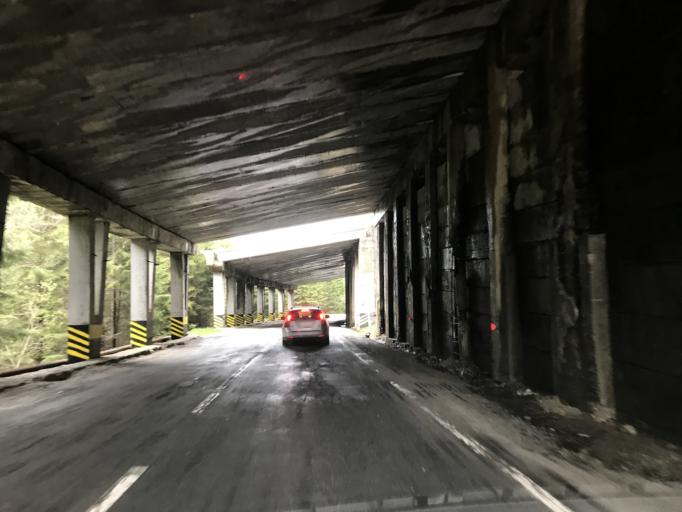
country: RO
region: Sibiu
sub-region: Comuna Cartisoara
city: Cartisoara
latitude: 45.6391
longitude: 24.6056
